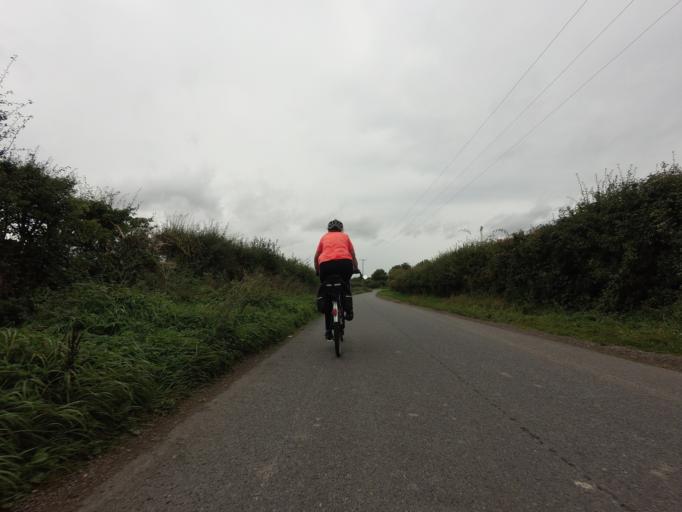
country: GB
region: England
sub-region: Cambridgeshire
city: Duxford
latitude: 52.0465
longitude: 0.1482
